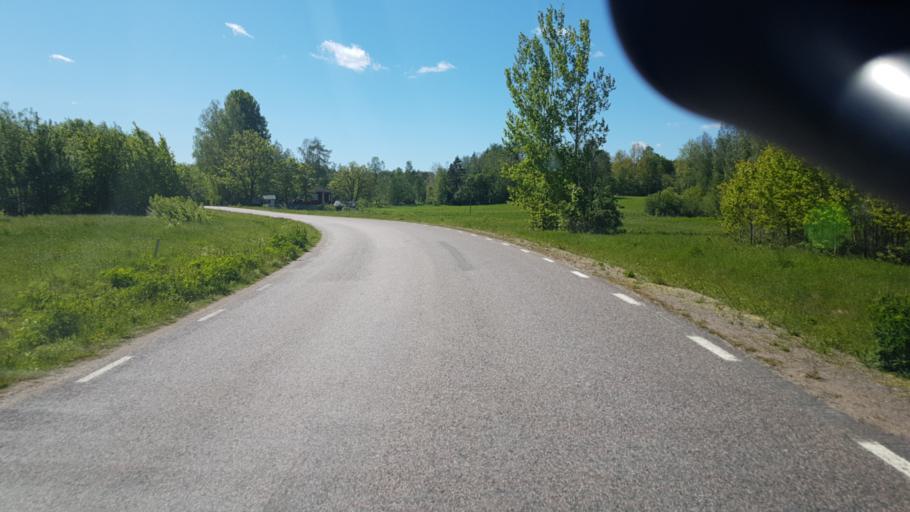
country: SE
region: Vaermland
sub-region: Grums Kommun
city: Slottsbron
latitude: 59.4670
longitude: 12.8760
